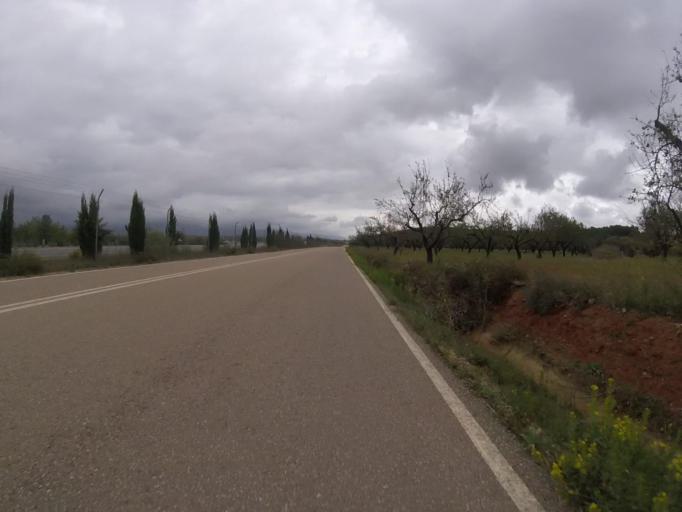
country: ES
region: Valencia
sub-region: Provincia de Castello
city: Cabanes
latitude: 40.1798
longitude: 0.0453
